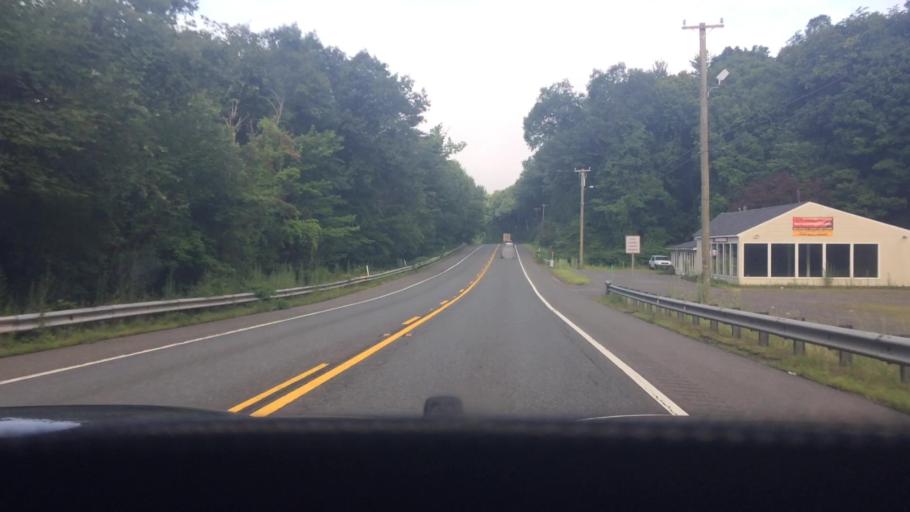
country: US
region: Massachusetts
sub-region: Franklin County
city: Millers Falls
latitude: 42.6080
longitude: -72.5103
